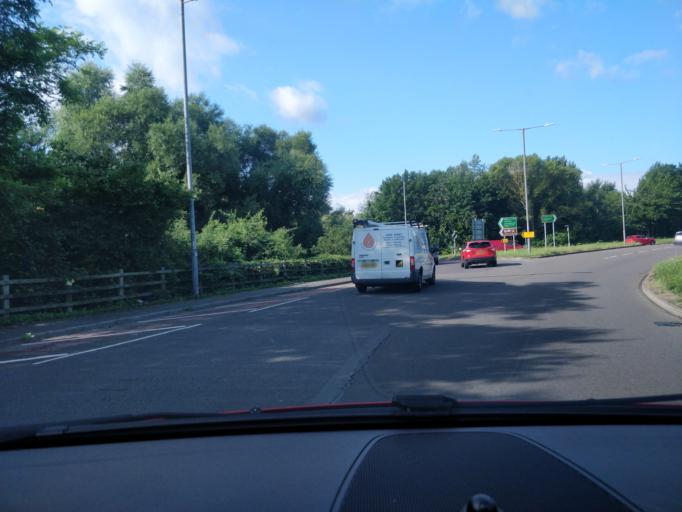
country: GB
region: Wales
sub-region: Conwy
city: Llansantffraid Glan Conwy
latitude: 53.2799
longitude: -3.7902
